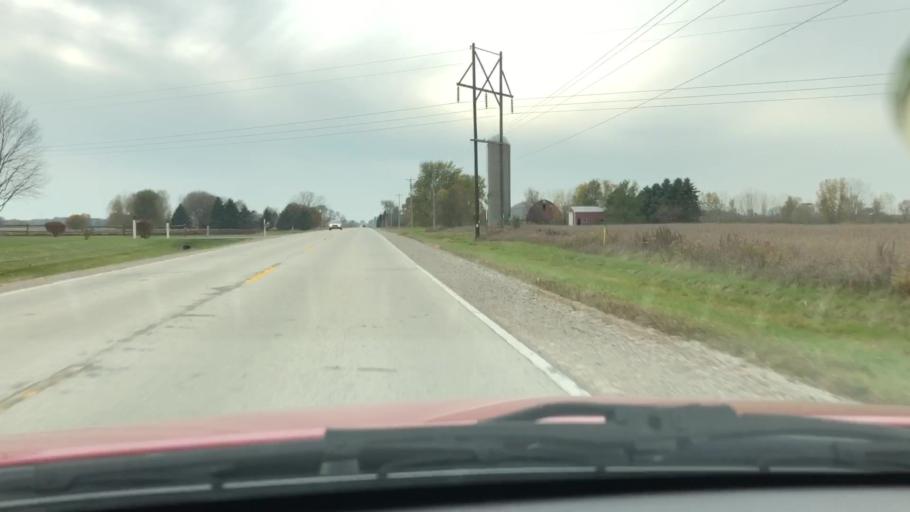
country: US
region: Wisconsin
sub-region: Outagamie County
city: Seymour
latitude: 44.4441
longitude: -88.2726
